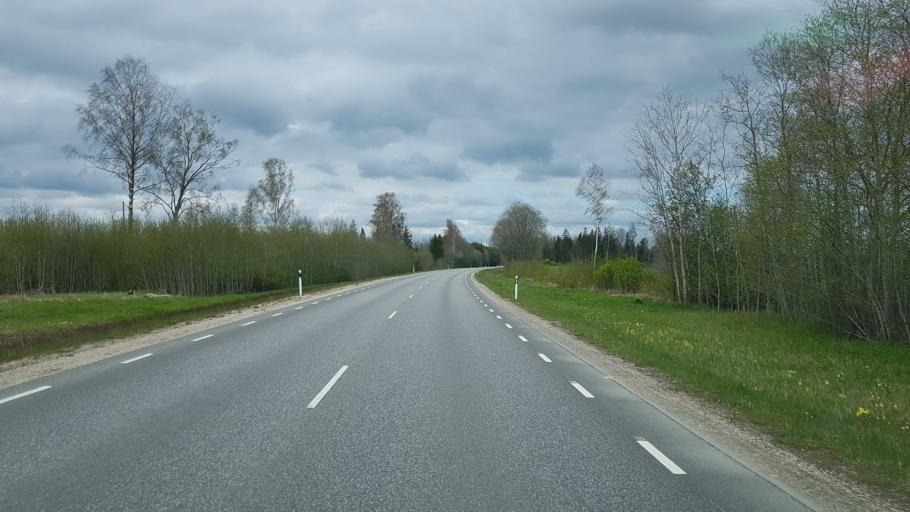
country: EE
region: Harju
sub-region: Anija vald
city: Kehra
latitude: 59.2226
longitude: 25.2627
